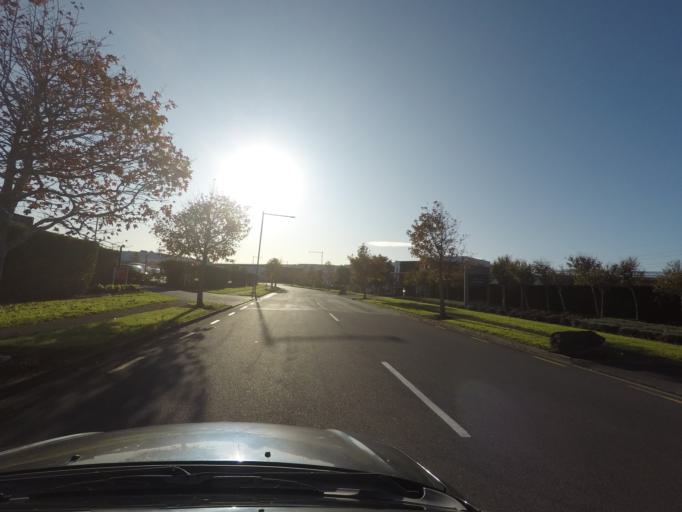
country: NZ
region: Auckland
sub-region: Auckland
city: Manukau City
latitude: -36.9416
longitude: 174.8772
